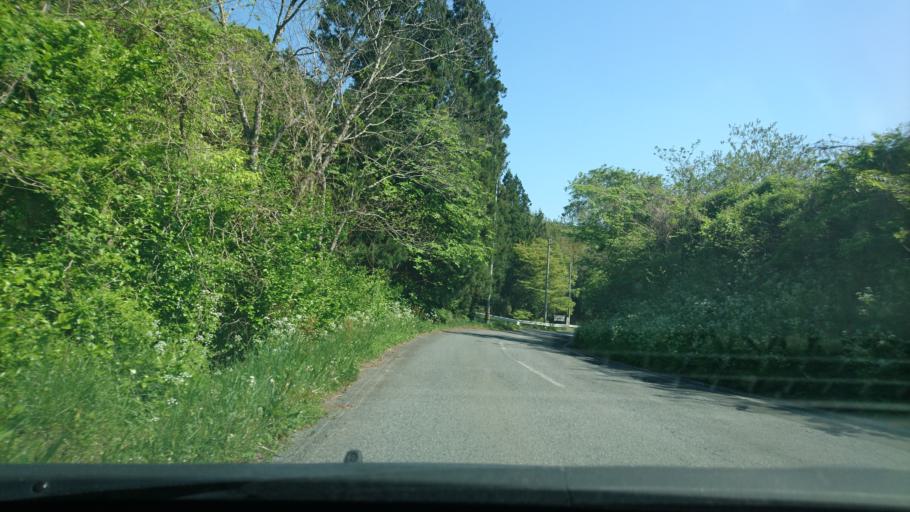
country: JP
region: Iwate
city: Ichinoseki
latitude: 38.9156
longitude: 141.2785
